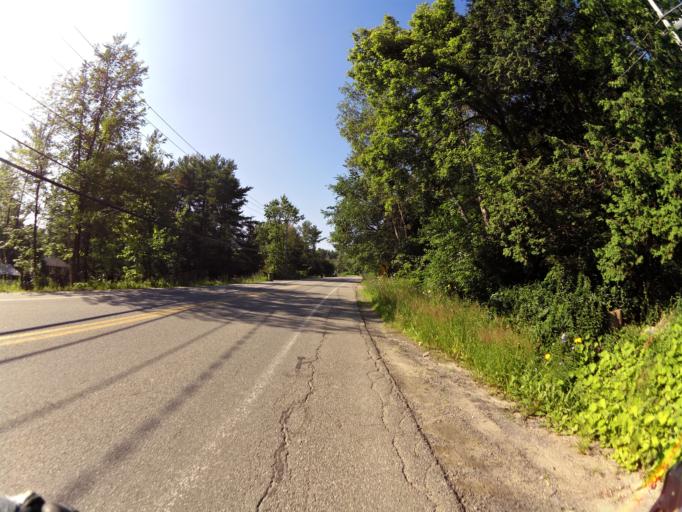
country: CA
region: Quebec
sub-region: Outaouais
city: Gatineau
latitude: 45.5300
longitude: -75.8049
